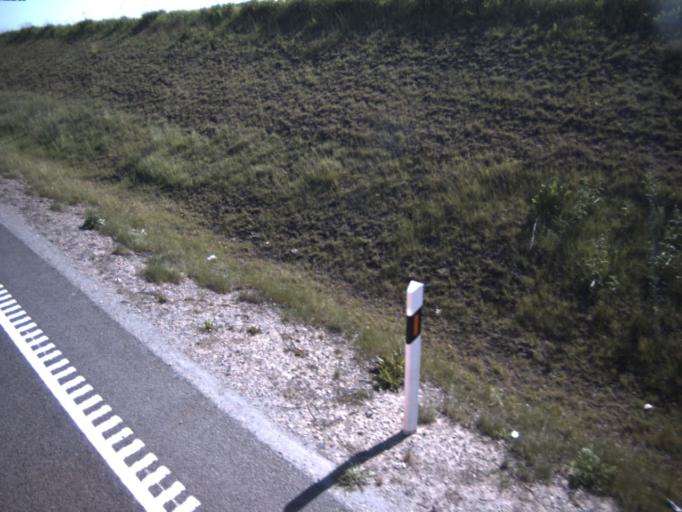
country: SE
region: Skane
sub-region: Helsingborg
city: Helsingborg
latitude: 56.0363
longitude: 12.7598
